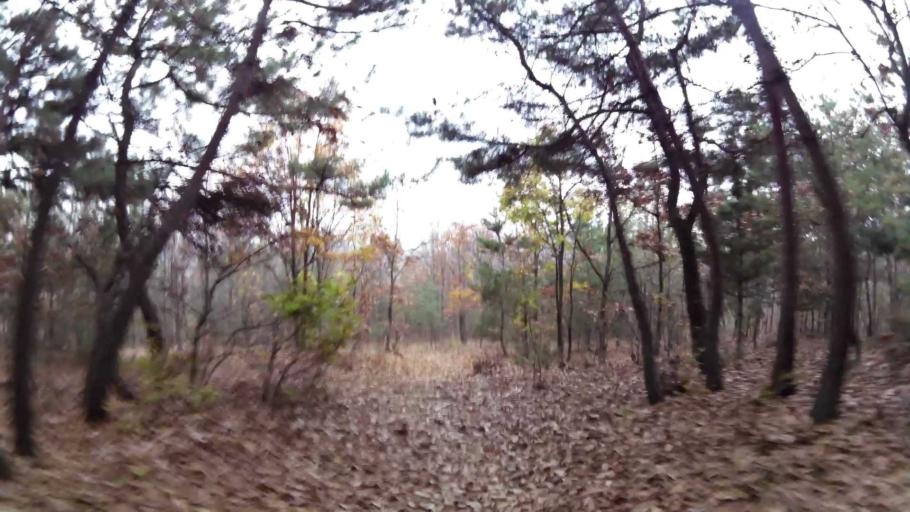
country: KR
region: Daegu
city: Daegu
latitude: 35.8619
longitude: 128.6680
